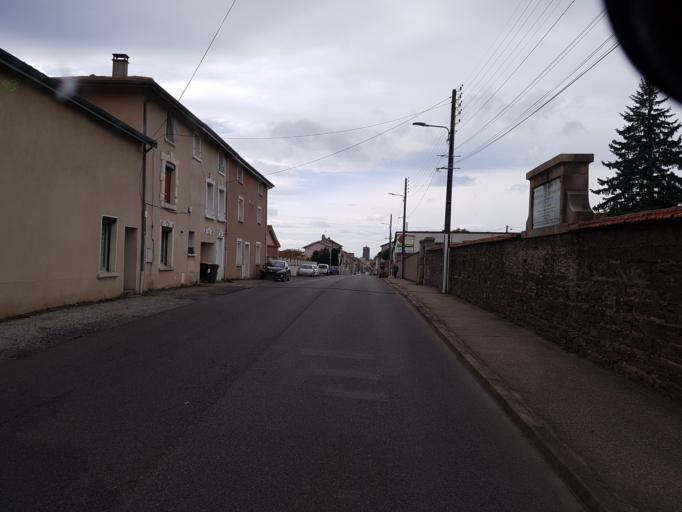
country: FR
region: Rhone-Alpes
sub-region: Departement de la Loire
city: Chazelles-sur-Lyon
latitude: 45.6422
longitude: 4.3968
